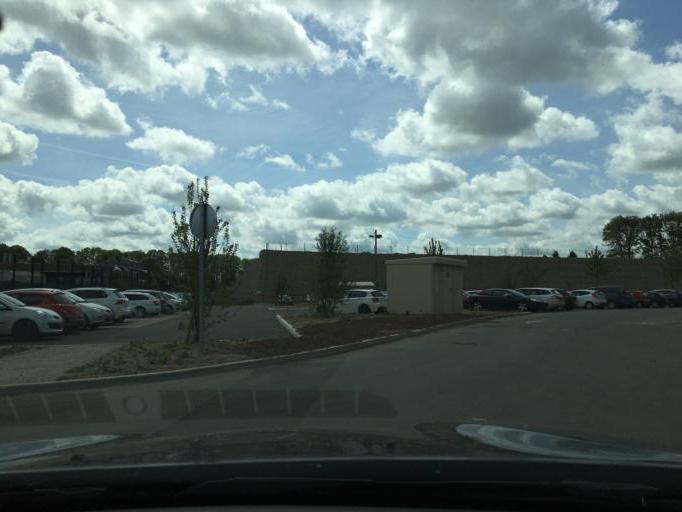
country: FR
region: Centre
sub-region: Departement du Loiret
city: Saran
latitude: 47.9601
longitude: 1.8846
